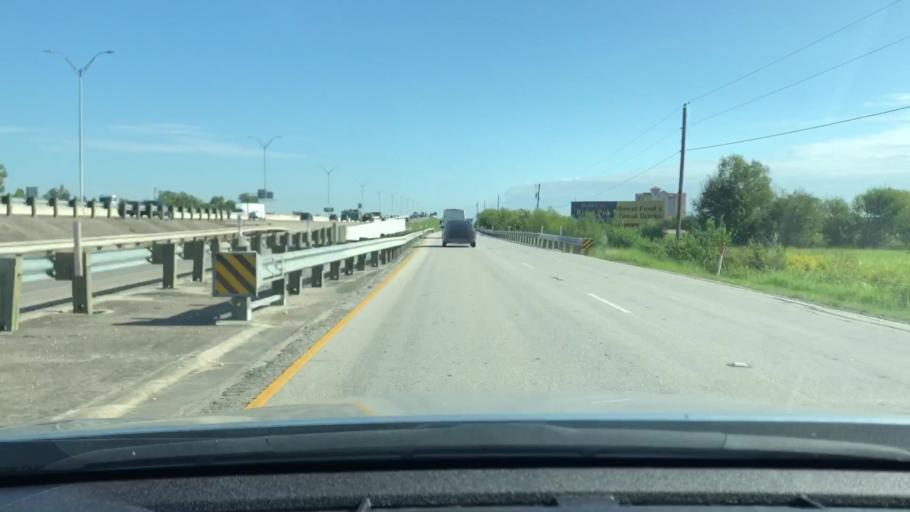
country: US
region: Texas
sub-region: Hays County
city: San Marcos
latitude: 29.8345
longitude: -97.9776
